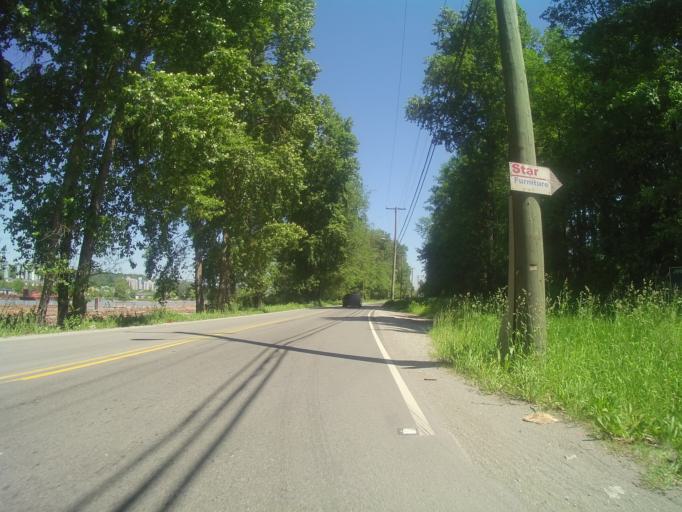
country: CA
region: British Columbia
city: Vancouver
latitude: 49.2029
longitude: -123.0580
